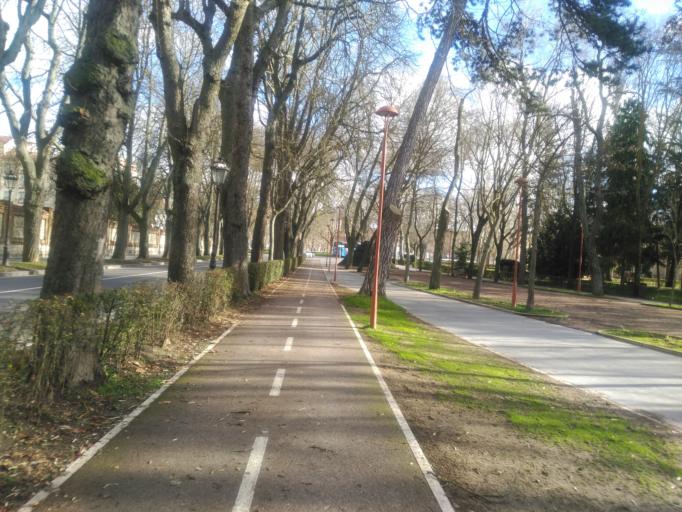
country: ES
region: Castille and Leon
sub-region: Provincia de Burgos
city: Burgos
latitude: 42.3383
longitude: -3.7103
